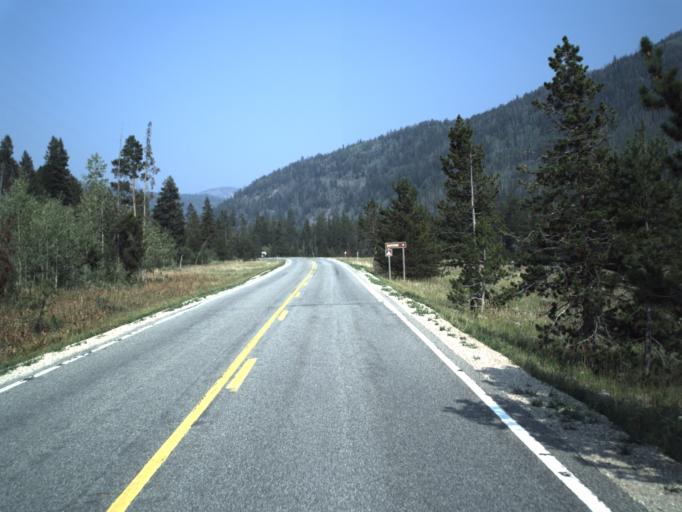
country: US
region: Utah
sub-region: Summit County
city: Francis
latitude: 40.5785
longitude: -111.0303
